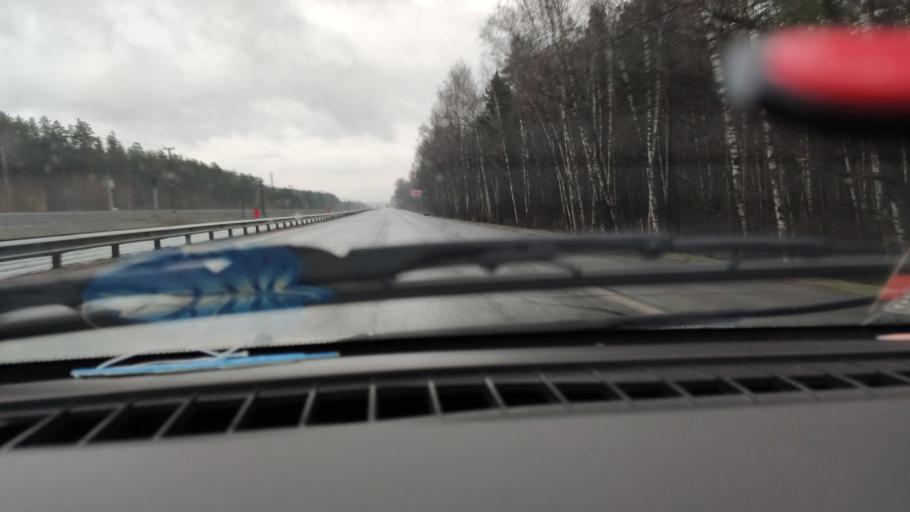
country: RU
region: Tatarstan
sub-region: Tukayevskiy Rayon
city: Naberezhnyye Chelny
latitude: 55.7401
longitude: 52.2494
